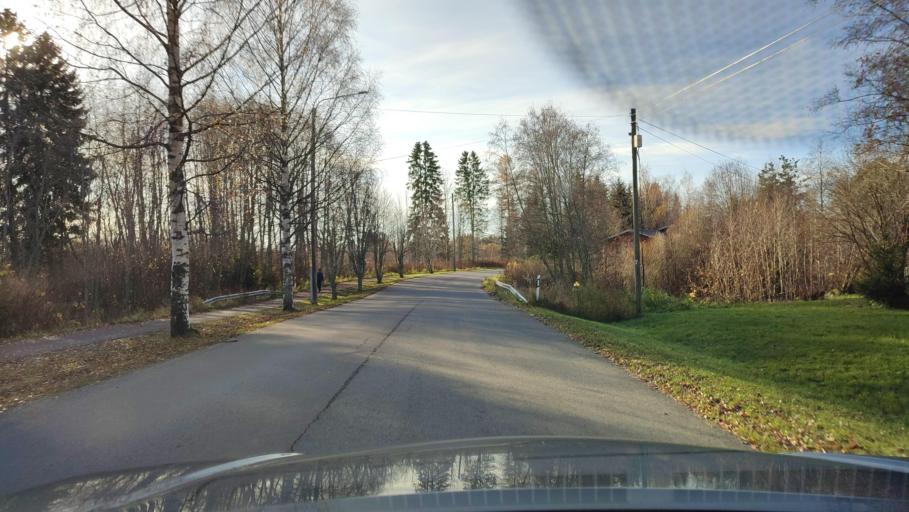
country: FI
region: Southern Ostrobothnia
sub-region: Suupohja
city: Teuva
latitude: 62.4770
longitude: 21.7465
